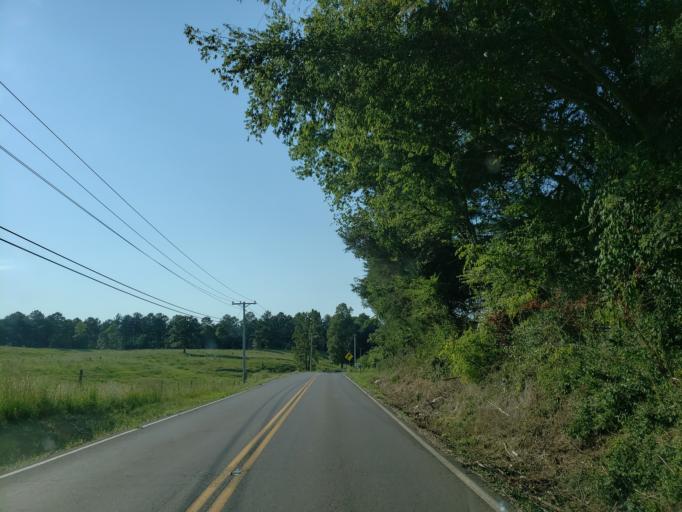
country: US
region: Tennessee
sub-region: Bradley County
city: Wildwood Lake
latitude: 35.0563
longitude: -84.7608
